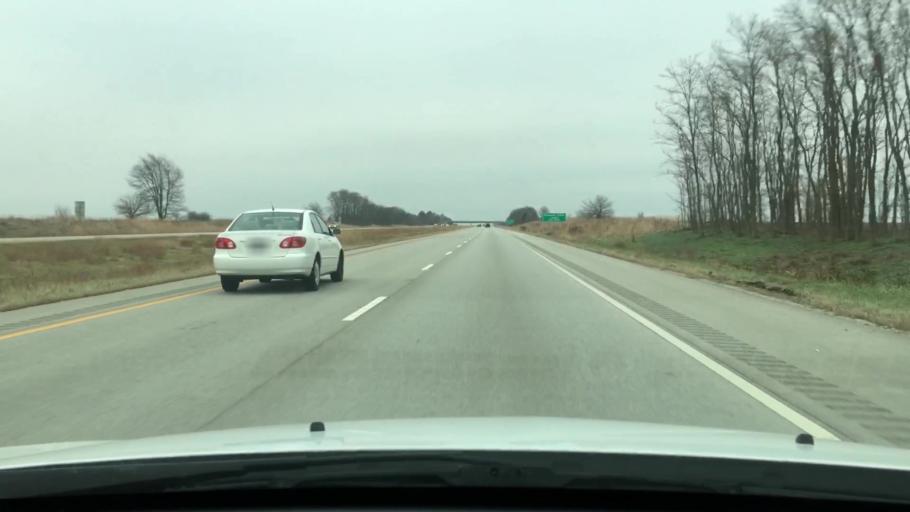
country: US
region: Illinois
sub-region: Sangamon County
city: New Berlin
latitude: 39.7398
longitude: -89.9378
